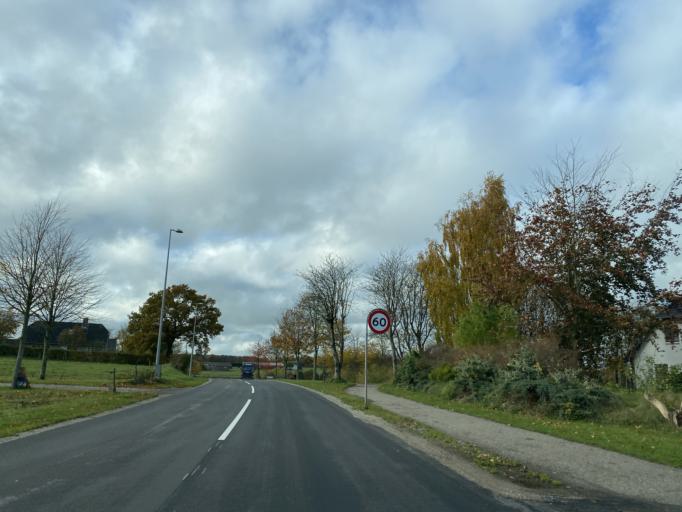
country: DK
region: Central Jutland
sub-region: Favrskov Kommune
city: Hammel
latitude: 56.2555
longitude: 9.8435
